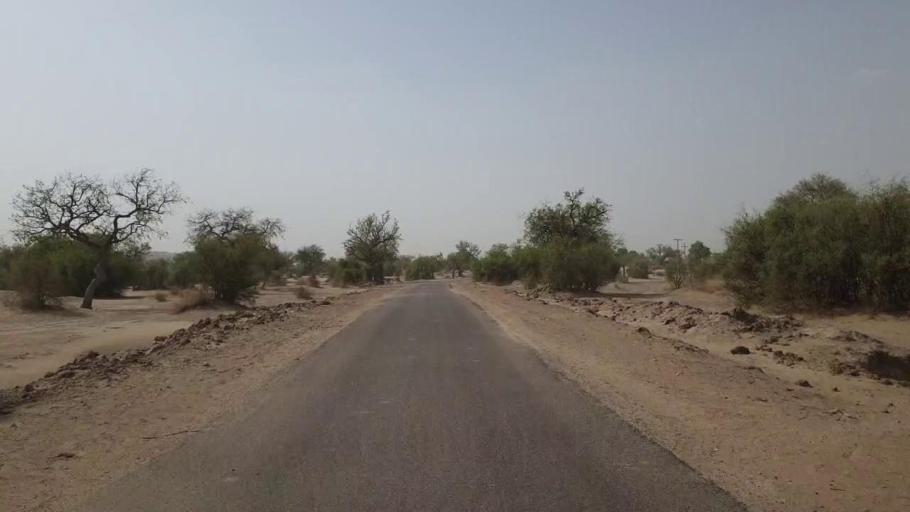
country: PK
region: Sindh
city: Mithi
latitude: 24.6082
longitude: 69.9209
